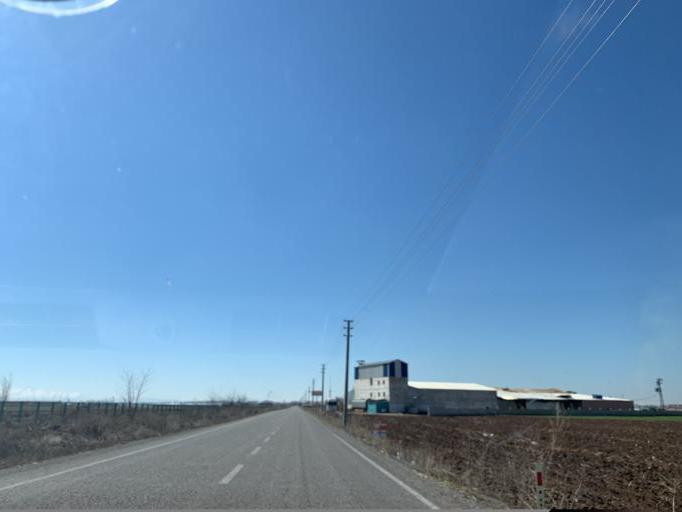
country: TR
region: Konya
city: Cumra
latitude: 37.5986
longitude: 32.7909
